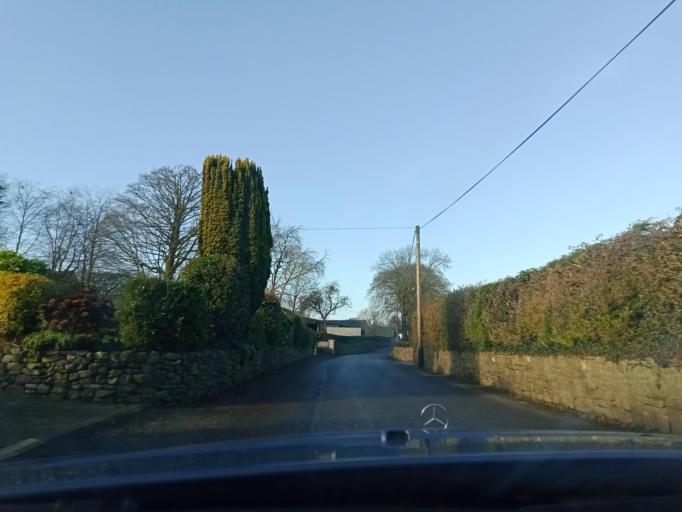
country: IE
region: Leinster
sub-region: Kilkenny
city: Callan
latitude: 52.4702
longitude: -7.4161
